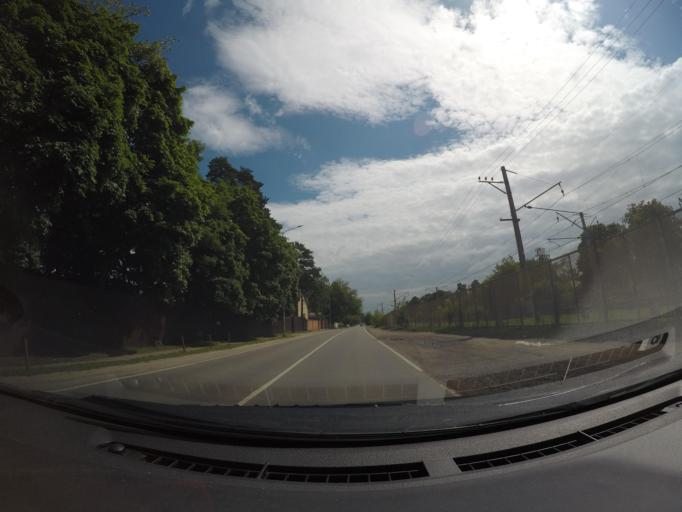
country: RU
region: Moskovskaya
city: Malakhovka
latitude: 55.6446
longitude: 38.0123
